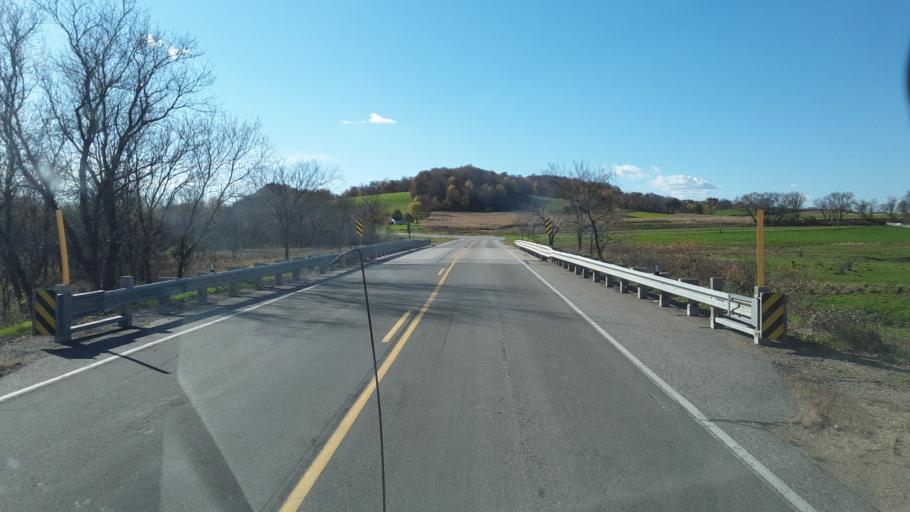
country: US
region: Wisconsin
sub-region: Sauk County
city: Reedsburg
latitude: 43.5406
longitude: -90.1691
